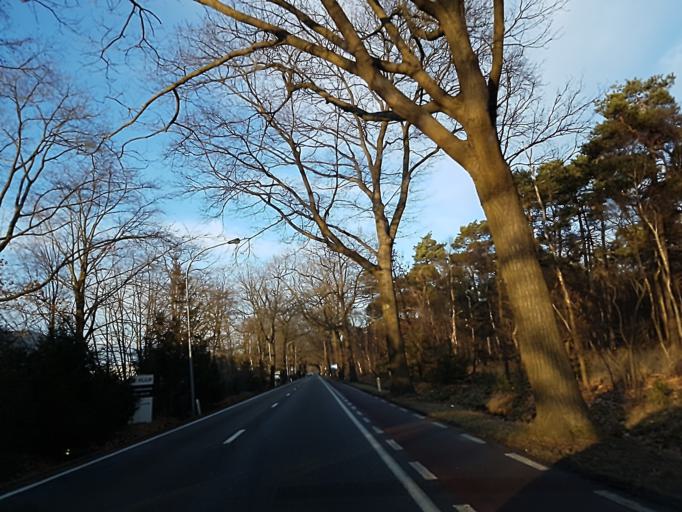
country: NL
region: North Brabant
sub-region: Gemeente Goirle
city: Goirle
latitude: 51.4662
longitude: 5.0461
